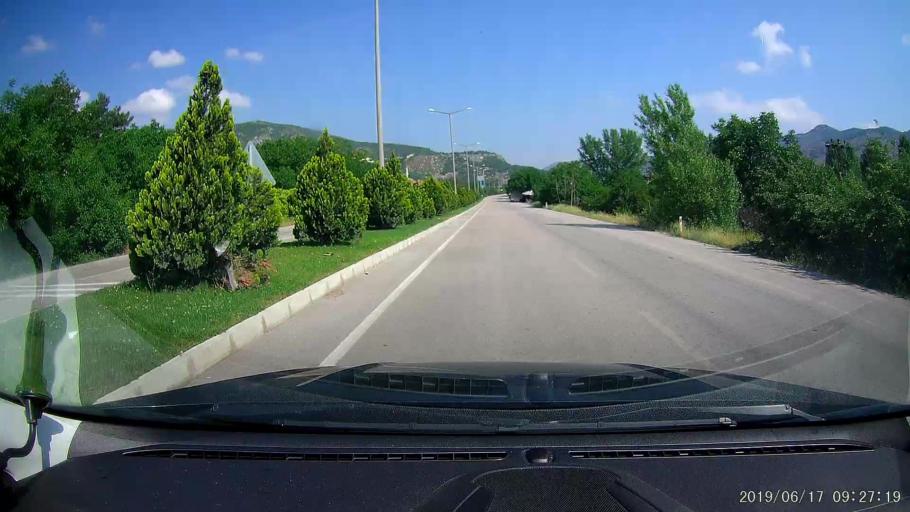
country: TR
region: Amasya
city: Amasya
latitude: 40.6759
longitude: 35.8275
